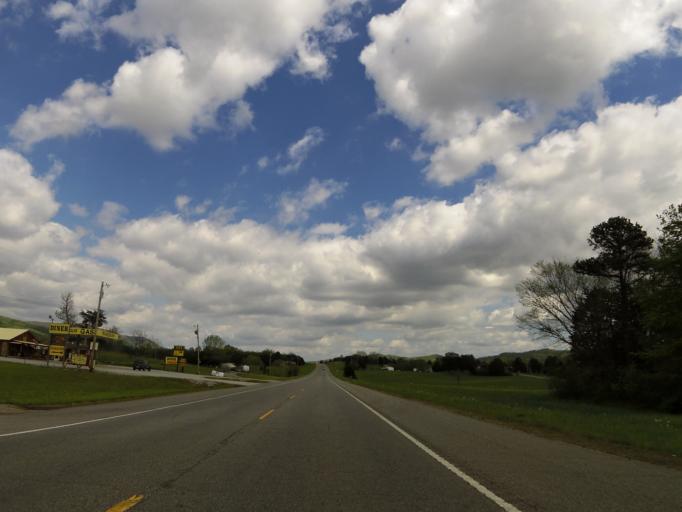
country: US
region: Tennessee
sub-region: Campbell County
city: Fincastle
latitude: 36.4458
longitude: -83.9556
